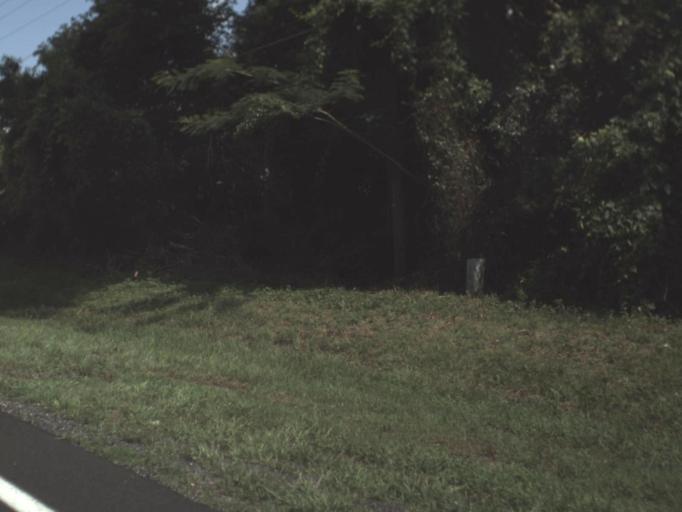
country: US
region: Florida
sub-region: Alachua County
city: Alachua
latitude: 29.7737
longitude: -82.4389
